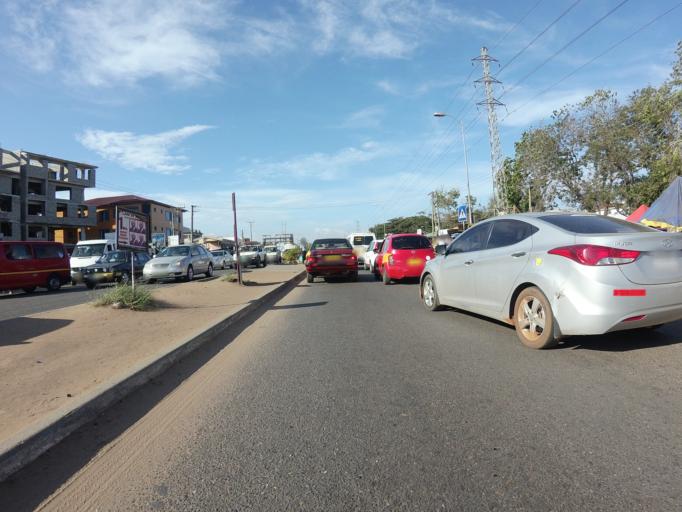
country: GH
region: Greater Accra
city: Nungua
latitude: 5.6225
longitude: -0.0698
